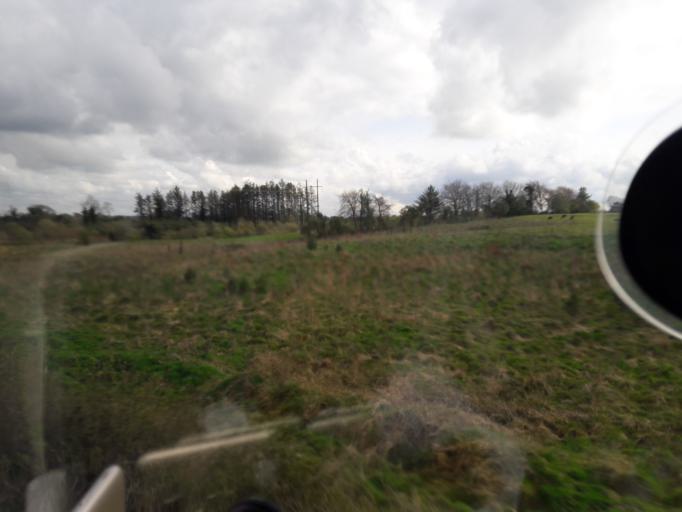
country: IE
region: Leinster
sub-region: An Iarmhi
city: An Muileann gCearr
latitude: 53.5031
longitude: -7.2733
